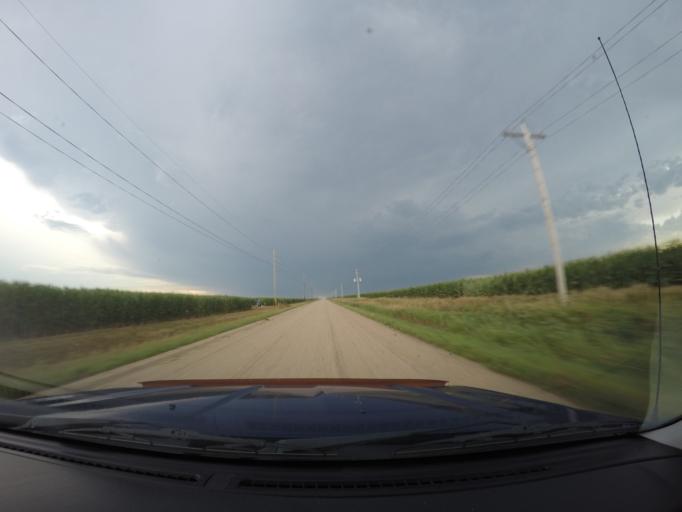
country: US
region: Nebraska
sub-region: Buffalo County
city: Kearney
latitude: 40.8437
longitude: -99.1673
